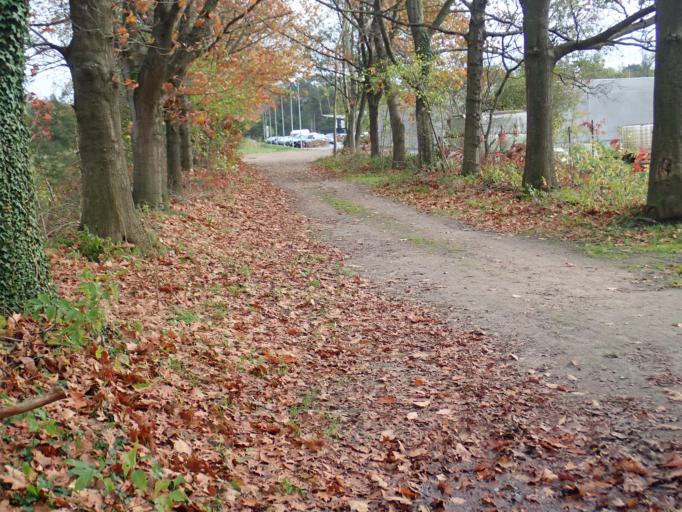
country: BE
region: Flanders
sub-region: Provincie Antwerpen
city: Zoersel
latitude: 51.2520
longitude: 4.7031
